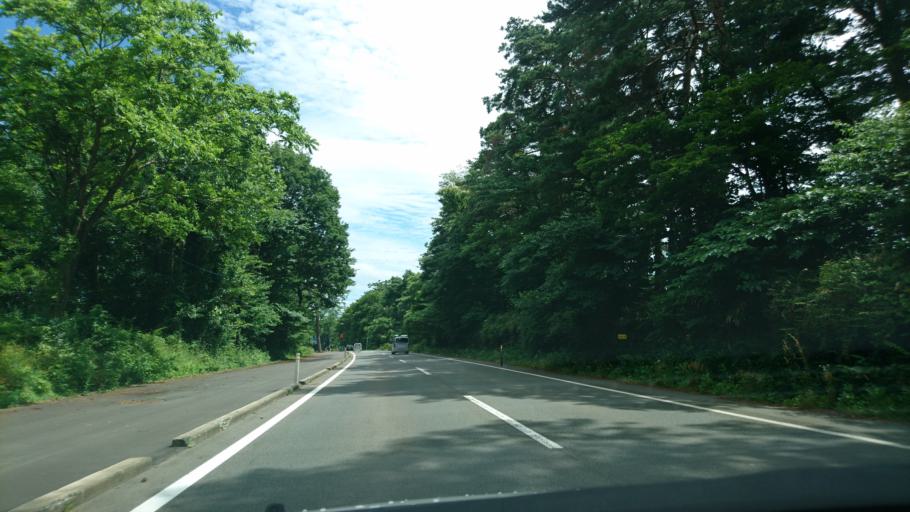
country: JP
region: Iwate
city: Morioka-shi
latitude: 39.7762
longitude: 141.1269
